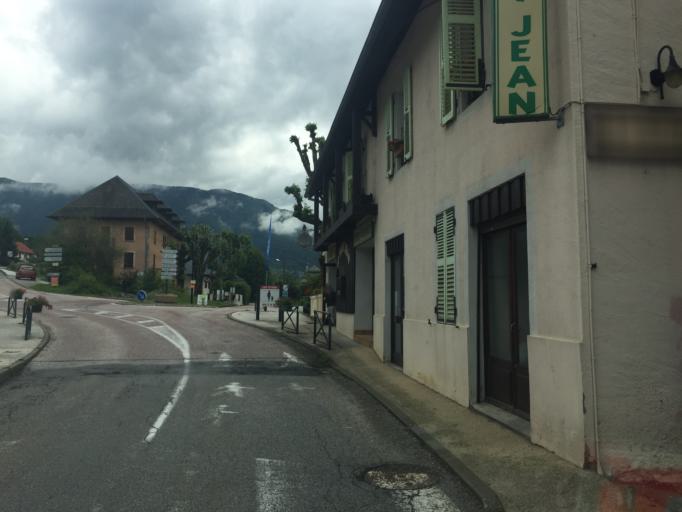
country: FR
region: Rhone-Alpes
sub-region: Departement de la Savoie
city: Barby
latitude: 45.5860
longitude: 5.9963
